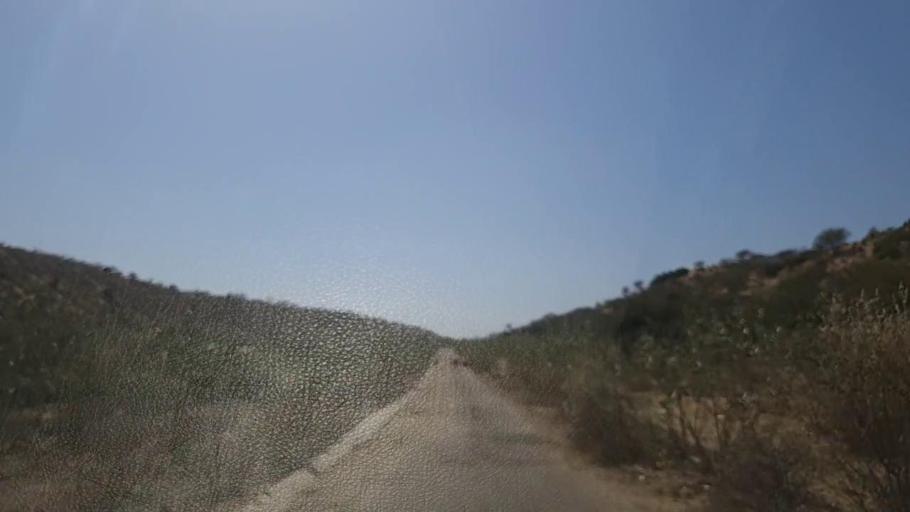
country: PK
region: Sindh
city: Naukot
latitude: 24.8297
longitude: 69.5835
